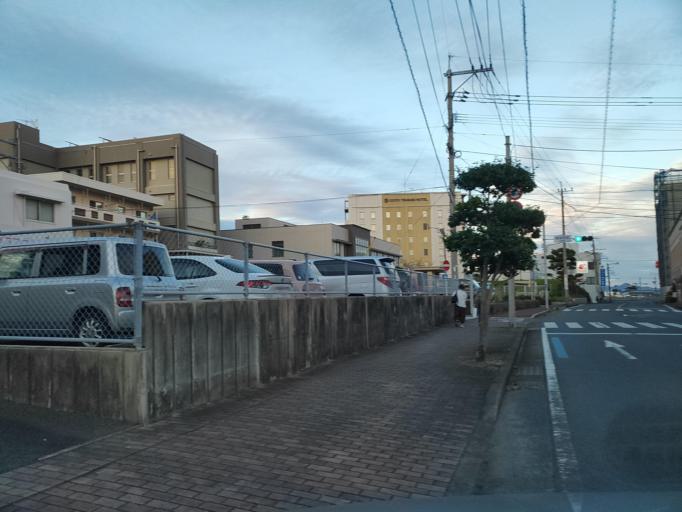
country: JP
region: Nagasaki
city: Fukuecho
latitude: 32.6952
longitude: 128.8461
